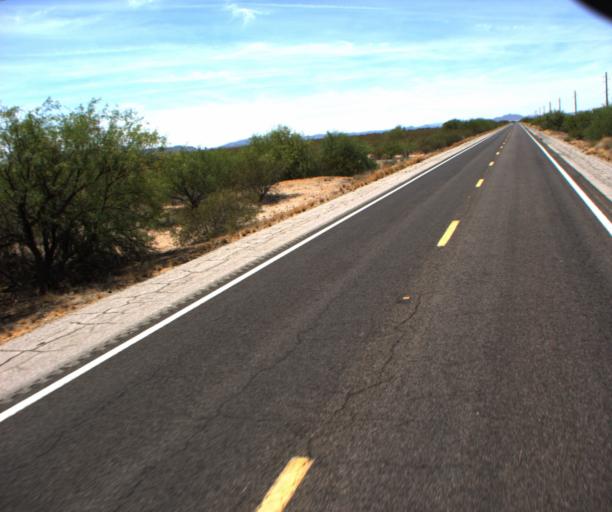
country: US
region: Arizona
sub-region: La Paz County
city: Salome
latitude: 33.8531
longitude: -113.4426
